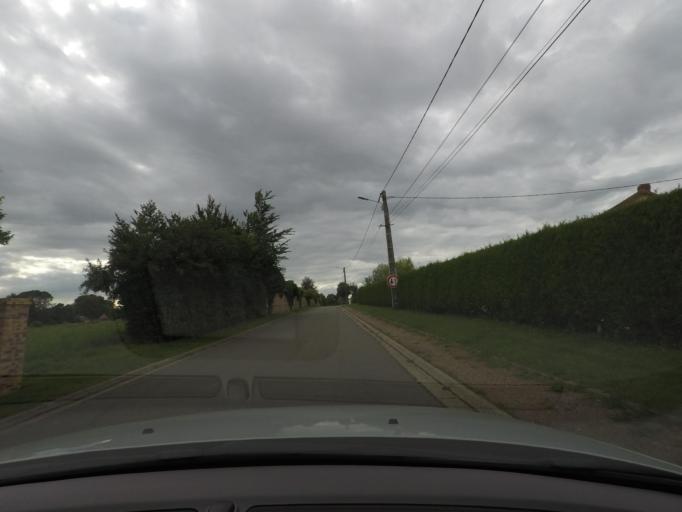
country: FR
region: Haute-Normandie
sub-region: Departement de l'Eure
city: Fleury-sur-Andelle
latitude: 49.2857
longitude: 1.3436
